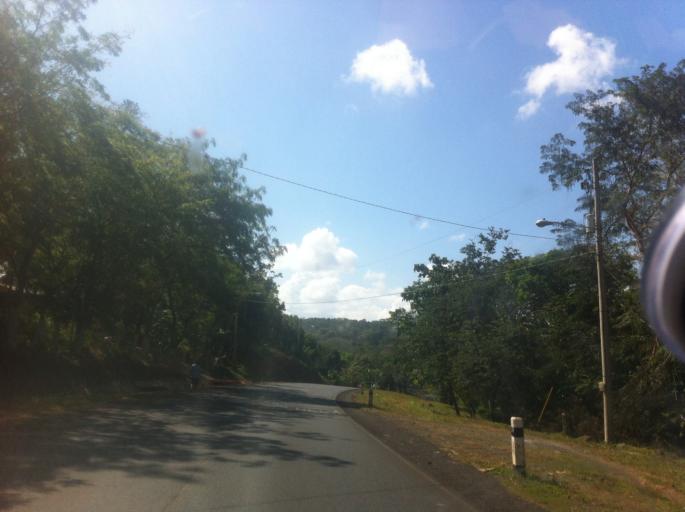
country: NI
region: Rio San Juan
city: San Carlos
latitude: 11.1771
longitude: -84.7427
